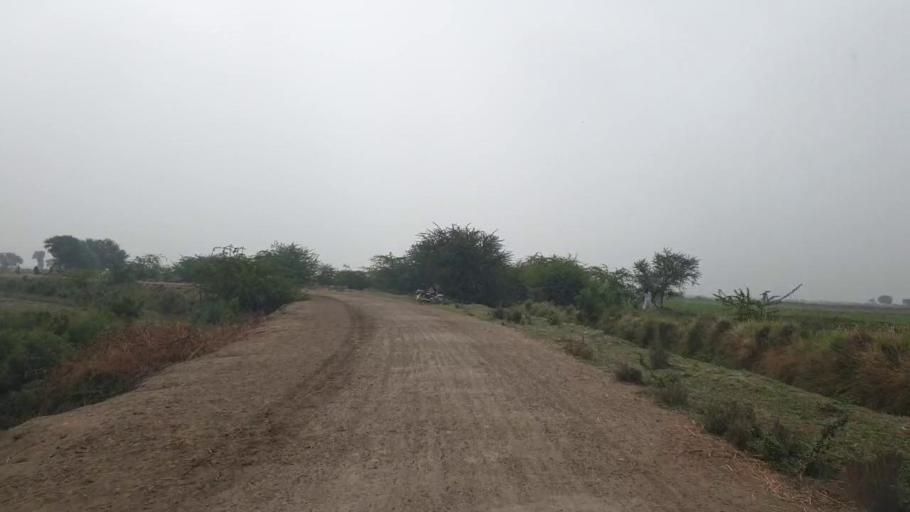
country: PK
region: Sindh
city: Badin
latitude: 24.5861
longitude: 68.6802
